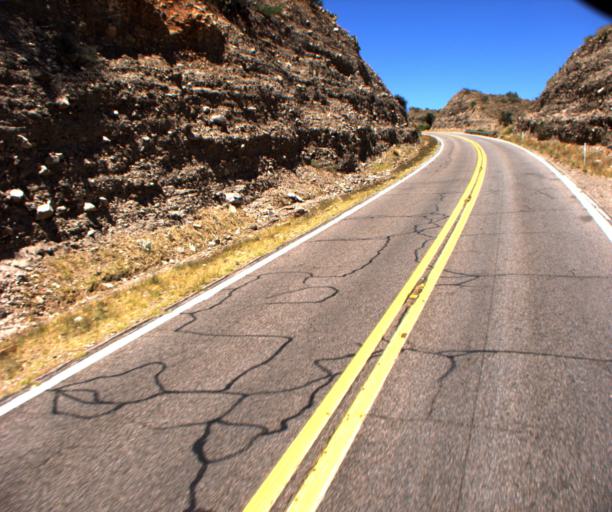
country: US
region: Arizona
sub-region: Pinal County
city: Kearny
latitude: 33.1713
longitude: -110.8083
